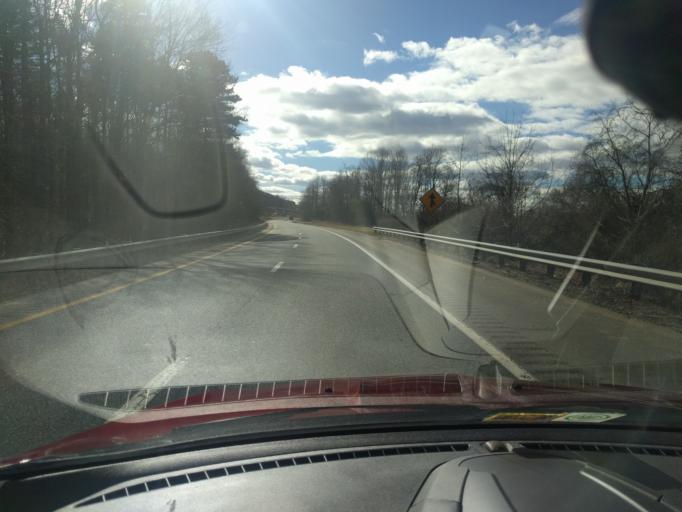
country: US
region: Virginia
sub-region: City of Lynchburg
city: West Lynchburg
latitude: 37.3612
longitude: -79.1663
